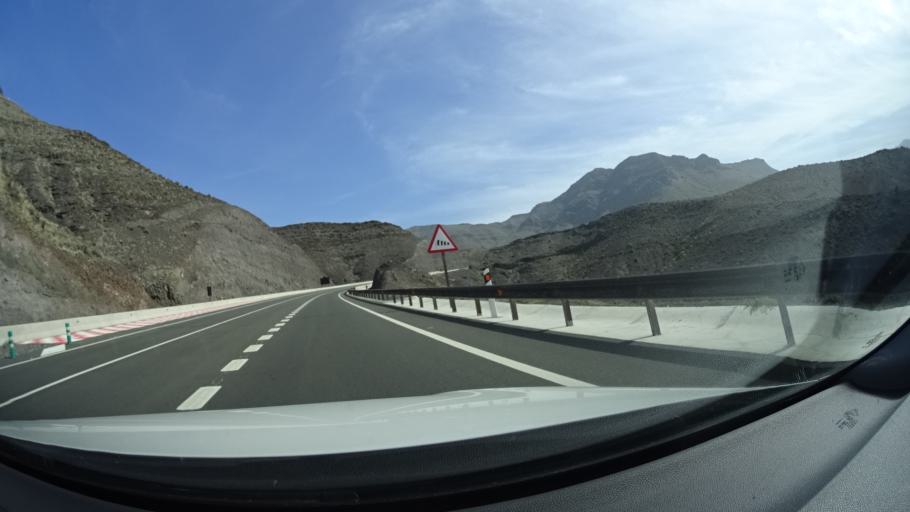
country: ES
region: Canary Islands
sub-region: Provincia de Las Palmas
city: San Nicolas
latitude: 28.0107
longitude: -15.7833
